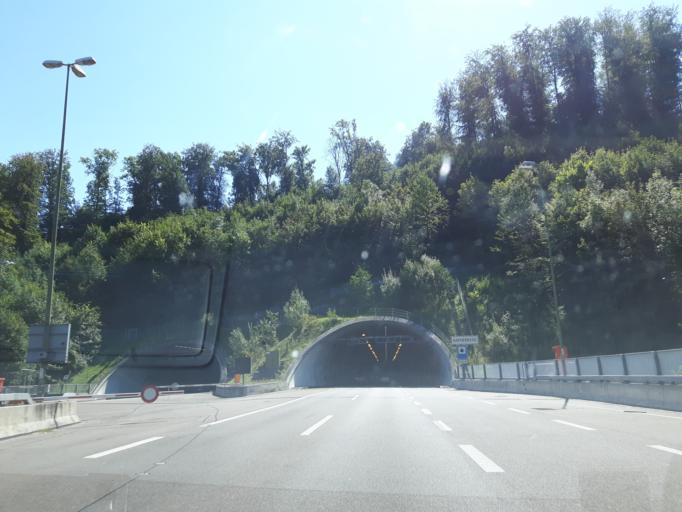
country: CH
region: Zurich
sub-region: Bezirk Dietikon
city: Urdorf / Oberurdorf
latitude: 47.3606
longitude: 8.4229
